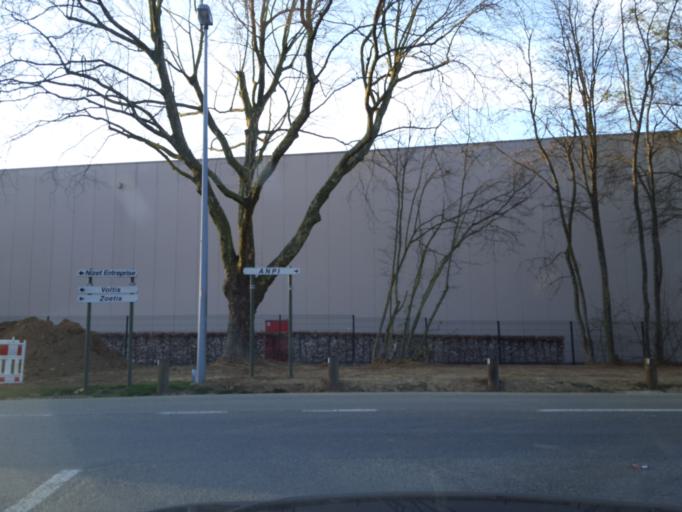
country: BE
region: Wallonia
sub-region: Province du Brabant Wallon
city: Louvain-la-Neuve
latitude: 50.6637
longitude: 4.6340
